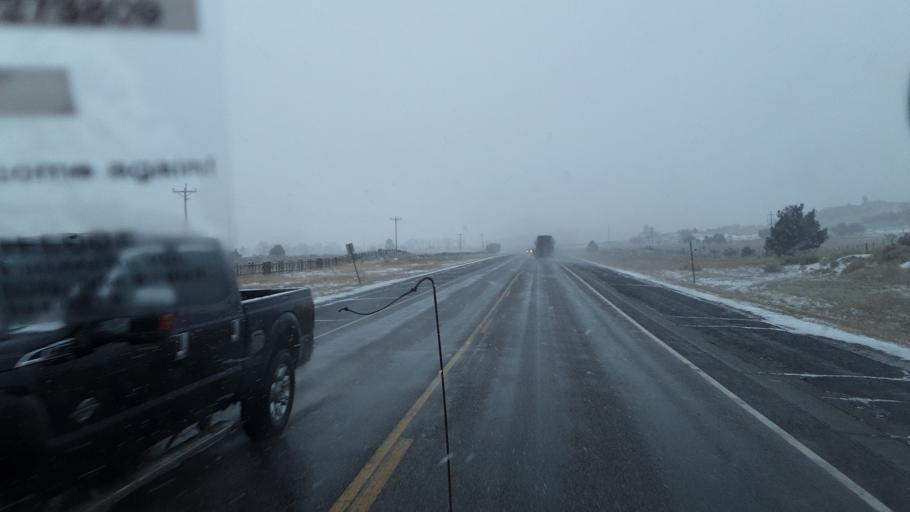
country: US
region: New Mexico
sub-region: Rio Arriba County
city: Chama
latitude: 36.8341
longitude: -106.5691
